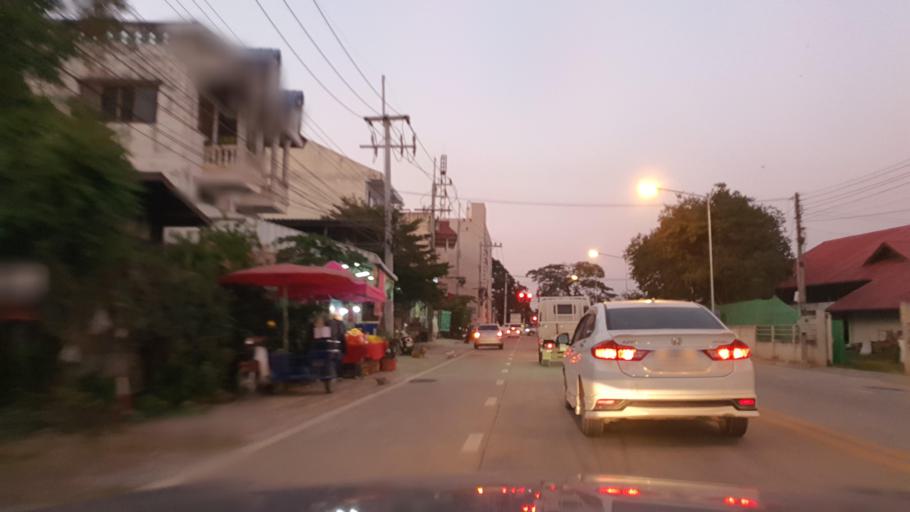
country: TH
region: Phayao
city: Dok Kham Tai
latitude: 19.1618
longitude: 99.9923
